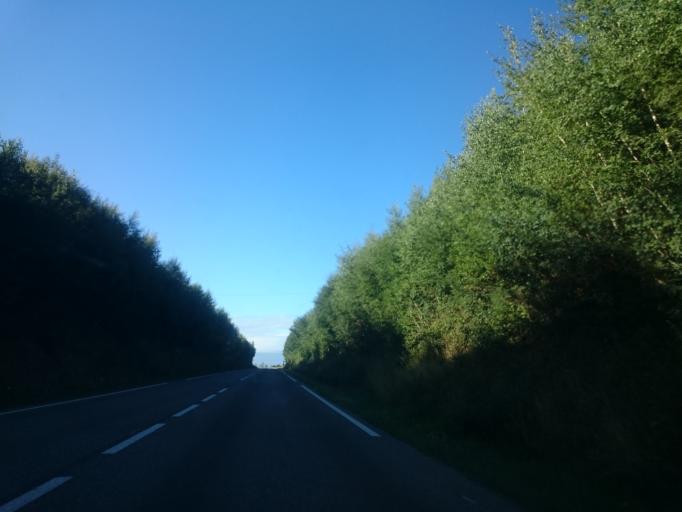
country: FR
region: Midi-Pyrenees
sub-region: Departement de l'Aveyron
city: Entraygues-sur-Truyere
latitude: 44.7322
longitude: 2.5085
